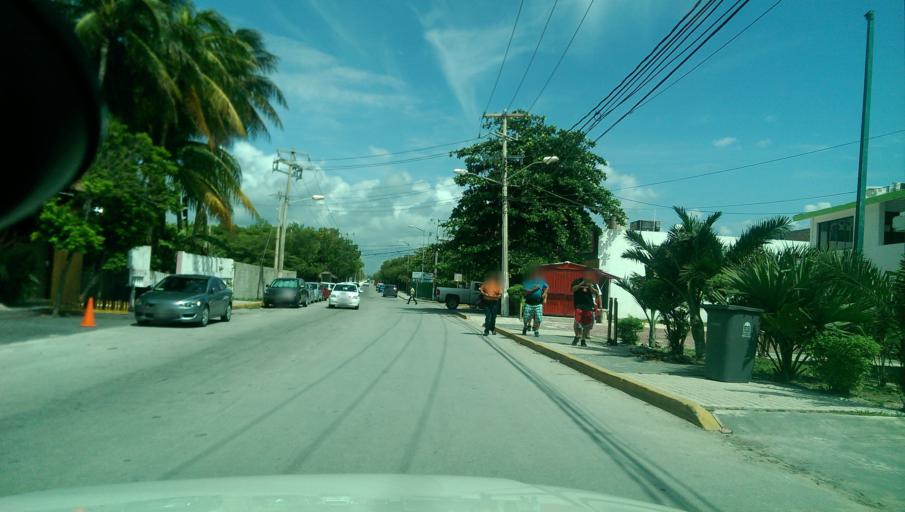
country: MX
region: Quintana Roo
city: Alfredo V. Bonfil
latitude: 20.8483
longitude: -86.8761
